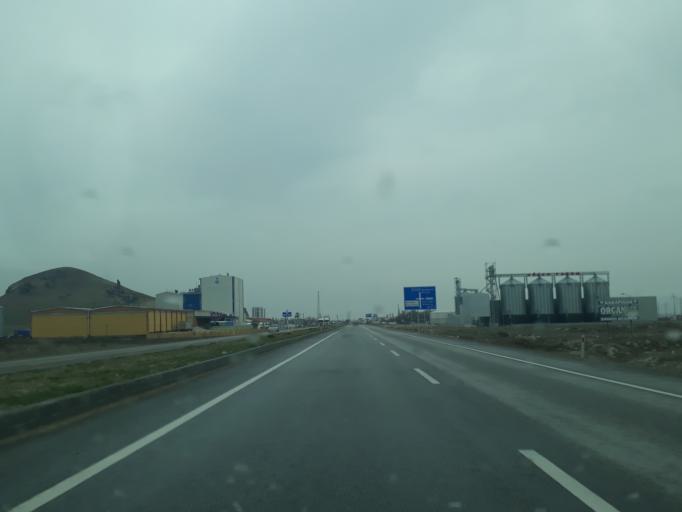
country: TR
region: Konya
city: Karapinar
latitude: 37.7142
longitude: 33.5889
